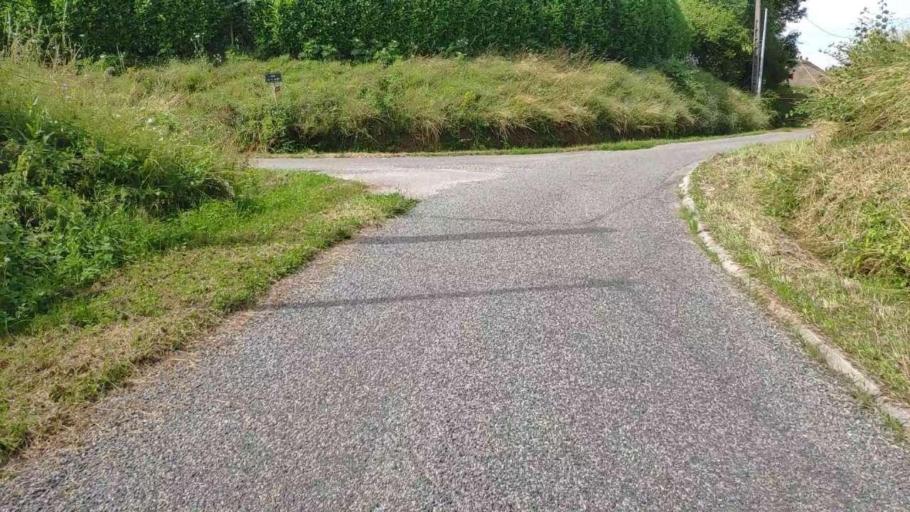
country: FR
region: Franche-Comte
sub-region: Departement du Jura
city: Bletterans
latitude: 46.8211
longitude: 5.4503
